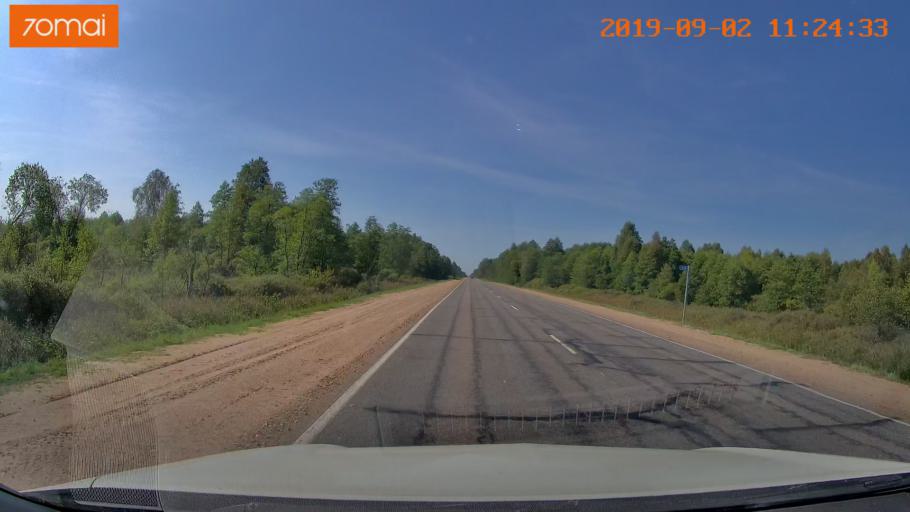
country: RU
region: Smolensk
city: Roslavl'
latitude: 54.0095
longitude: 32.9731
